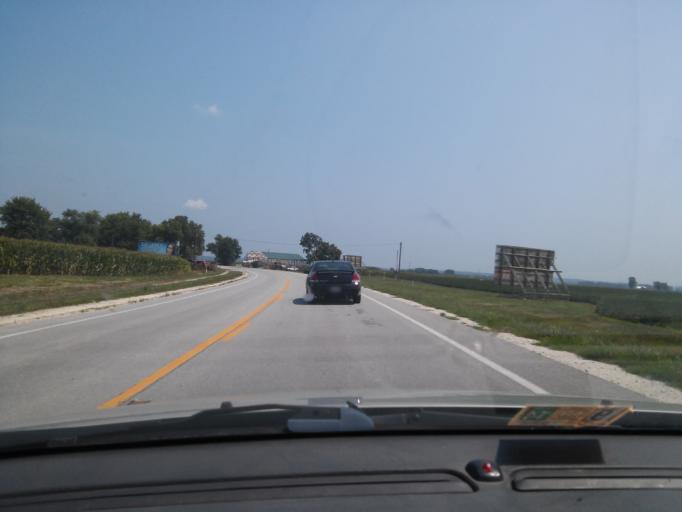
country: US
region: Missouri
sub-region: Pike County
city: Louisiana
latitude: 39.4609
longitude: -91.0328
